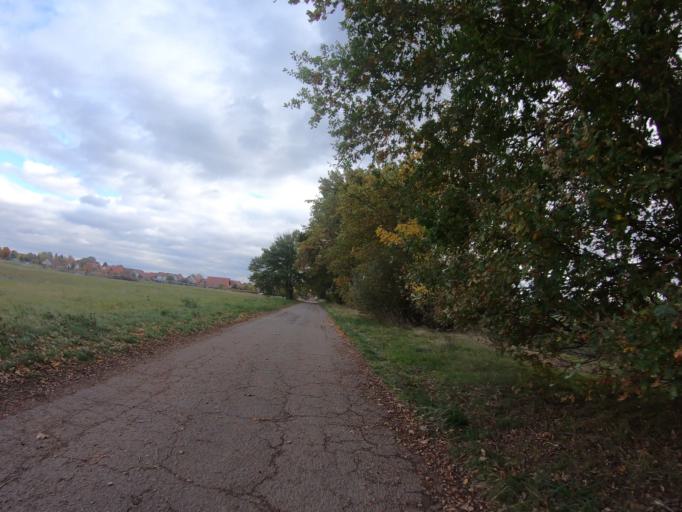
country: DE
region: Lower Saxony
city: Vordorf
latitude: 52.3677
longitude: 10.5133
